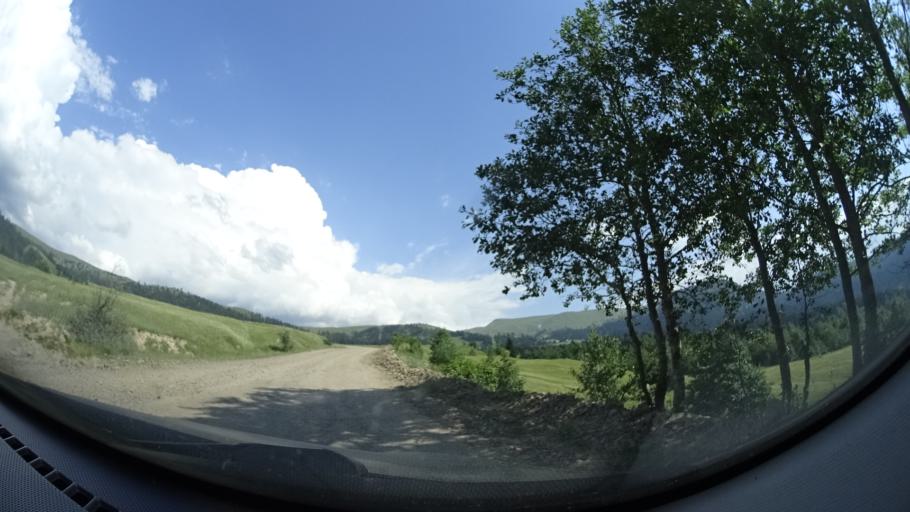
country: GE
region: Ajaria
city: Dioknisi
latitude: 41.6459
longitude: 42.4854
